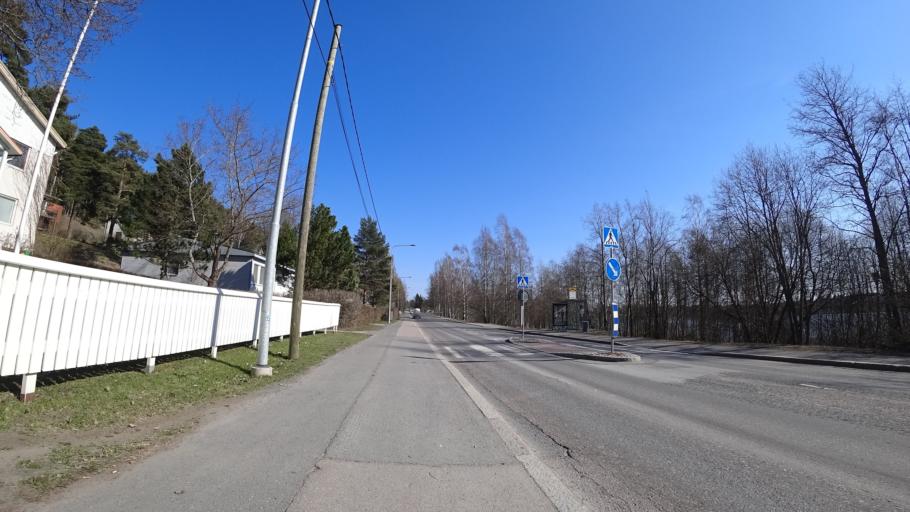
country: FI
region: Pirkanmaa
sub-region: Tampere
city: Pirkkala
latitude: 61.5130
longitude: 23.6561
